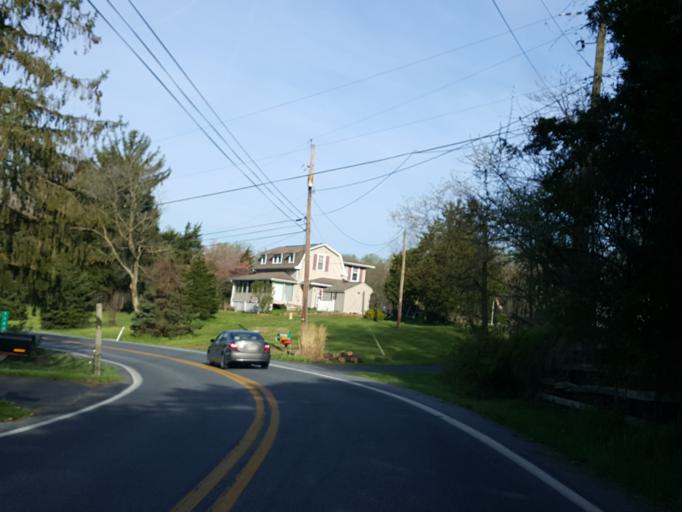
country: US
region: Pennsylvania
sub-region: Lebanon County
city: Annville
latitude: 40.2505
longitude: -76.4995
